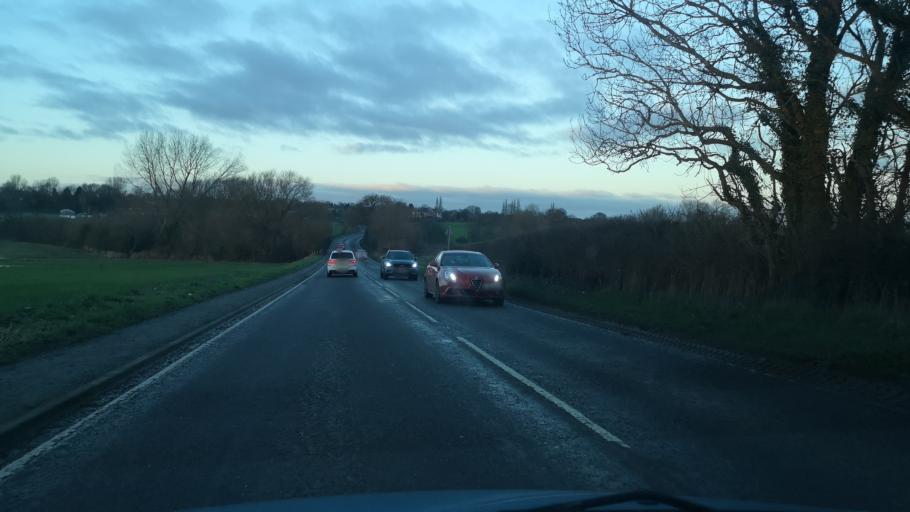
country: GB
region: England
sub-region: City and Borough of Wakefield
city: Low Ackworth
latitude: 53.6329
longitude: -1.3358
